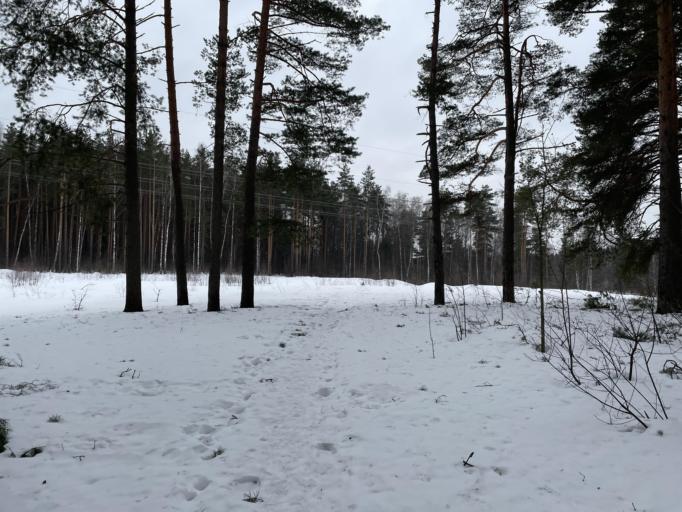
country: RU
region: Vladimir
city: Pokrov
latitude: 55.9414
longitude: 39.2373
